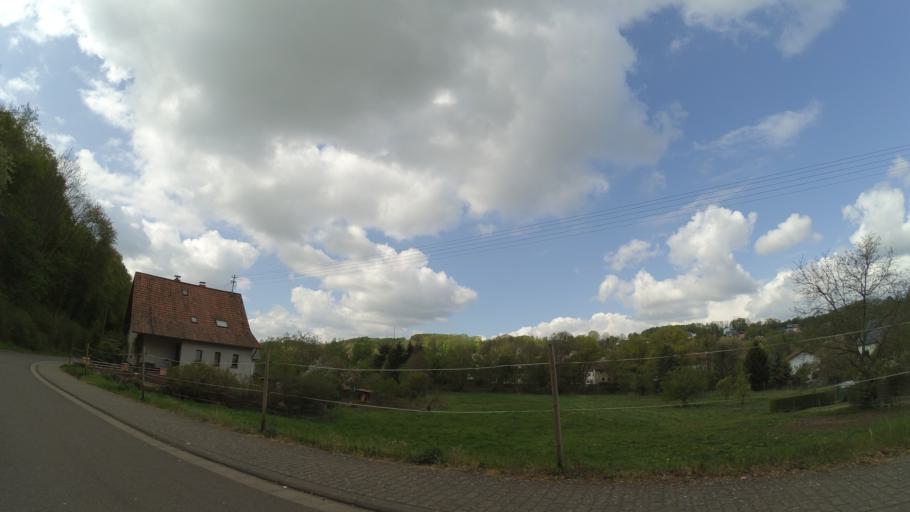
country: DE
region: Saarland
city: Wadern
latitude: 49.4947
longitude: 6.8709
